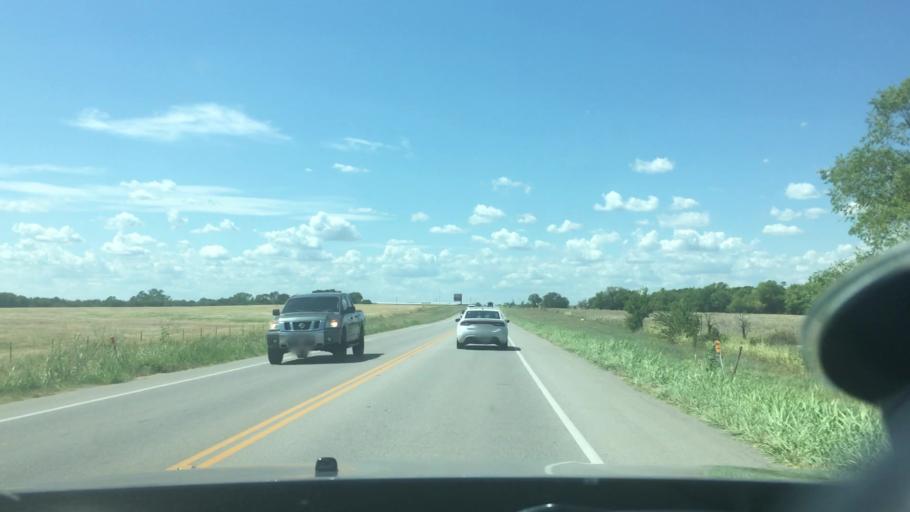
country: US
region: Oklahoma
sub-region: Marshall County
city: Kingston
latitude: 34.0424
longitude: -96.7367
